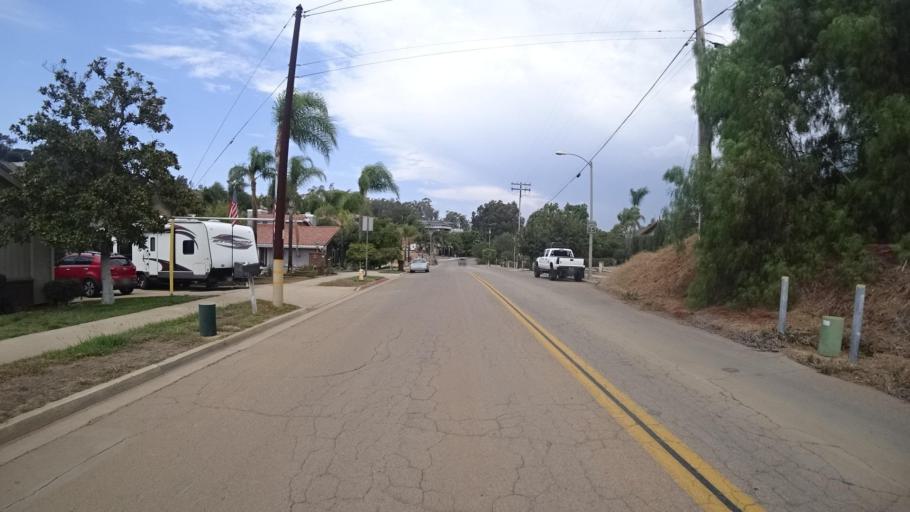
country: US
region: California
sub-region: San Diego County
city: Escondido
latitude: 33.1588
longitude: -117.1093
